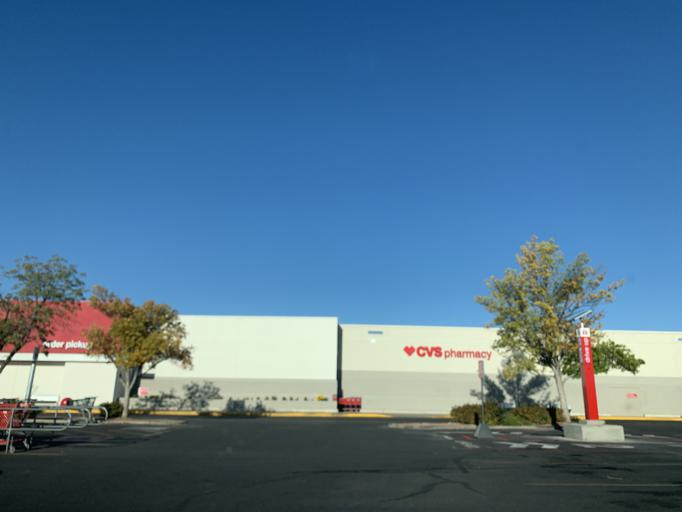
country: US
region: Colorado
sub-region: Mesa County
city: Redlands
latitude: 39.0931
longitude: -108.6007
